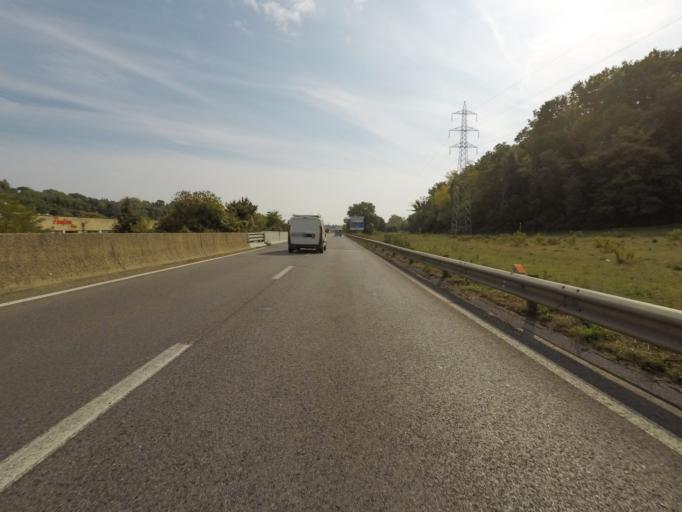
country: IT
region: Tuscany
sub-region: Provincia di Siena
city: Siena
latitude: 43.3037
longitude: 11.3200
